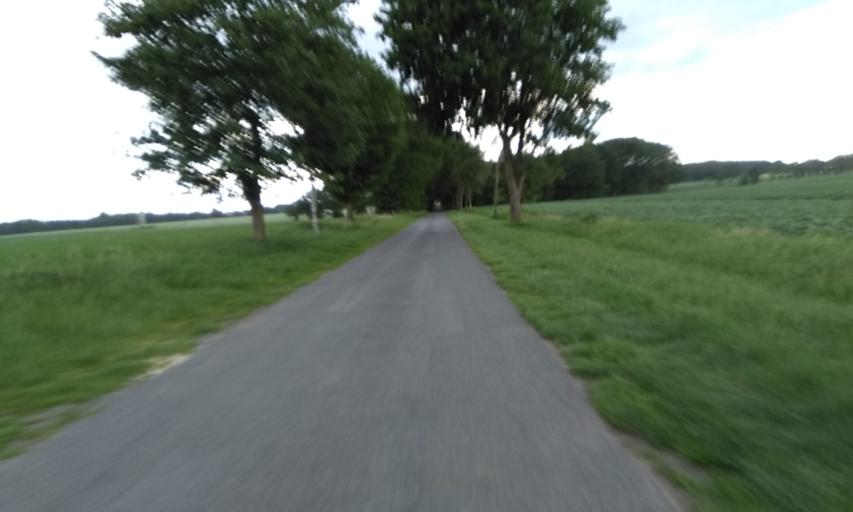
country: DE
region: Lower Saxony
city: Regesbostel
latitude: 53.3828
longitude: 9.6353
